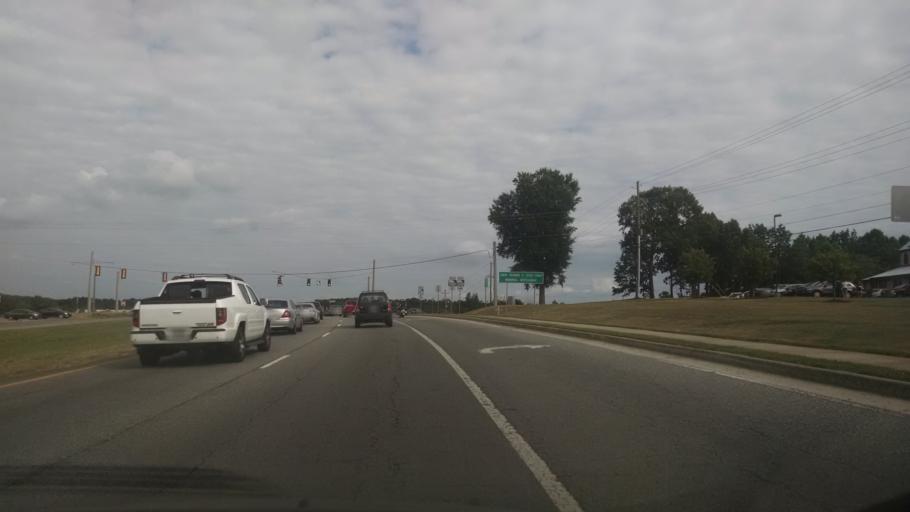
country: US
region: Georgia
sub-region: Forsyth County
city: Cumming
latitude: 34.1854
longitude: -84.1407
